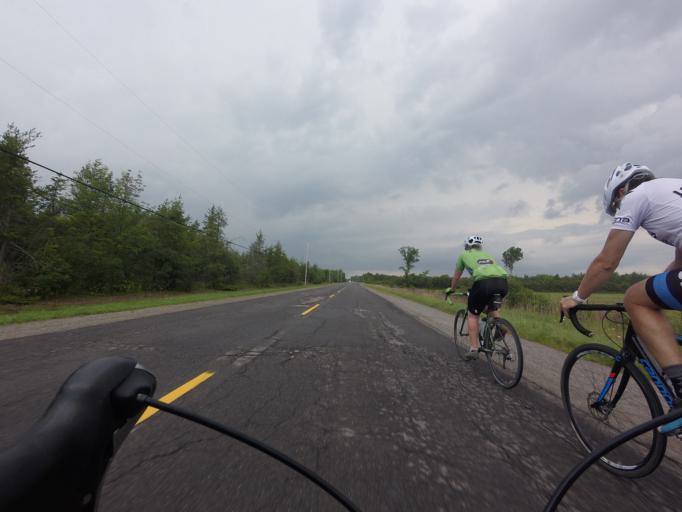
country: CA
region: Ontario
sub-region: Lanark County
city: Smiths Falls
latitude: 44.8835
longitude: -75.8174
